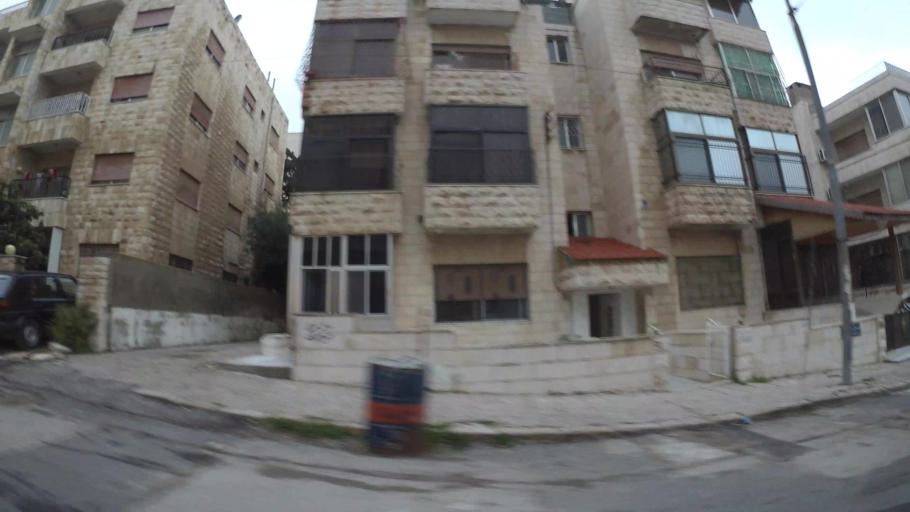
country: JO
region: Amman
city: Amman
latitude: 31.9667
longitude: 35.8846
